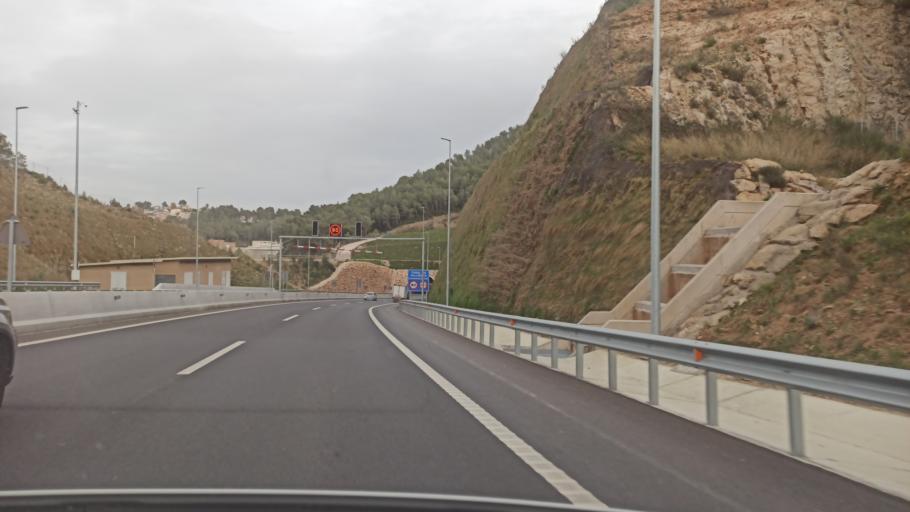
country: ES
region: Catalonia
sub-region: Provincia de Barcelona
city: Vallirana
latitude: 41.3810
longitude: 1.9247
